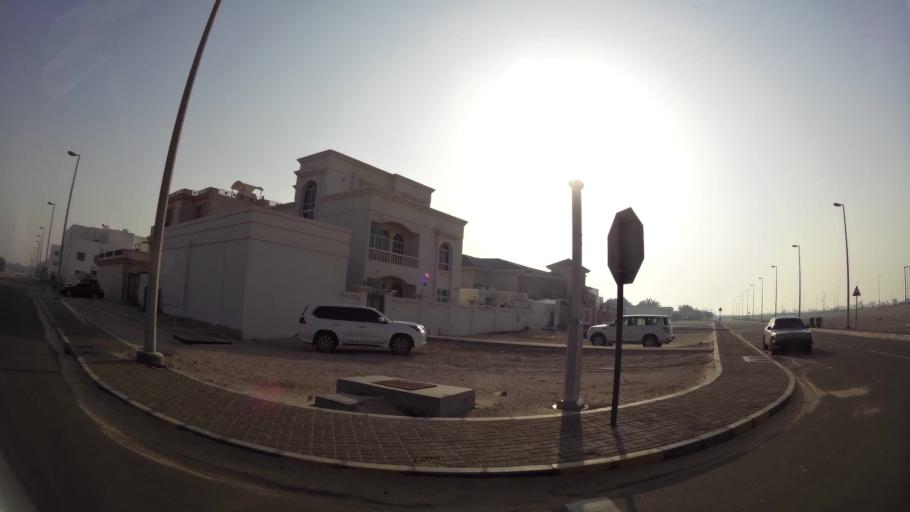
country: AE
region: Abu Dhabi
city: Abu Dhabi
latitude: 24.2786
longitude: 54.6401
